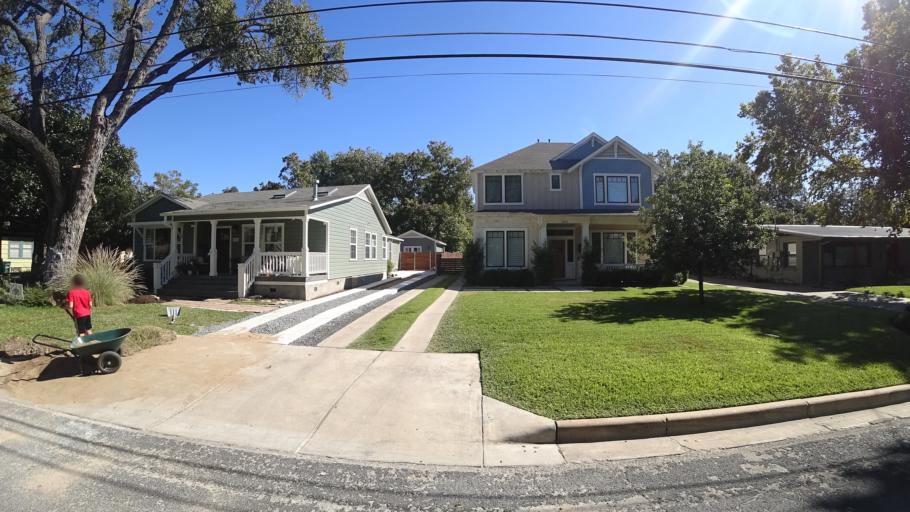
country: US
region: Texas
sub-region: Travis County
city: Austin
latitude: 30.3322
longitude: -97.7444
